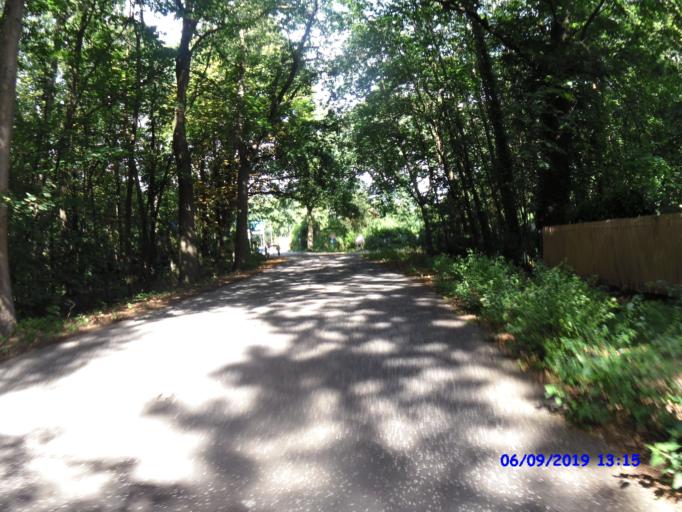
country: BE
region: Flanders
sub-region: Provincie Antwerpen
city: Geel
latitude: 51.2103
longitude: 5.0395
